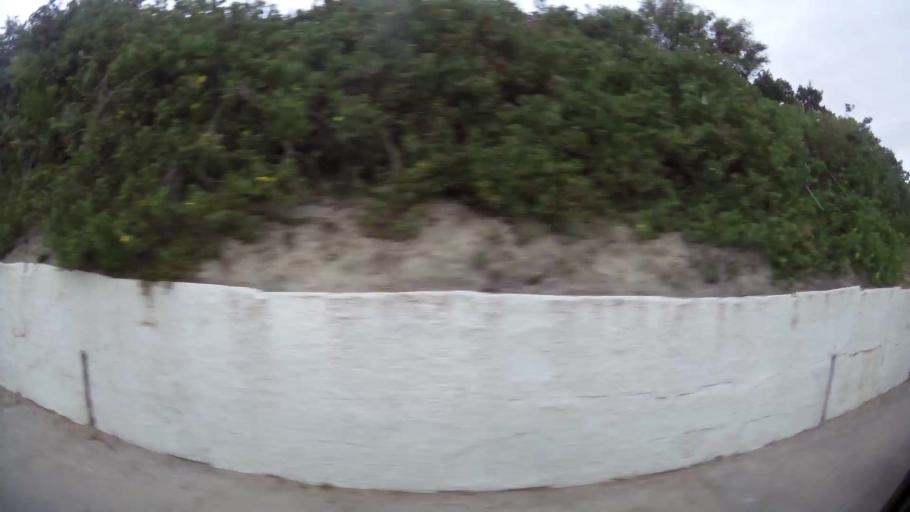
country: ZA
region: Eastern Cape
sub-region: Nelson Mandela Bay Metropolitan Municipality
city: Port Elizabeth
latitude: -33.9339
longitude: 25.5457
